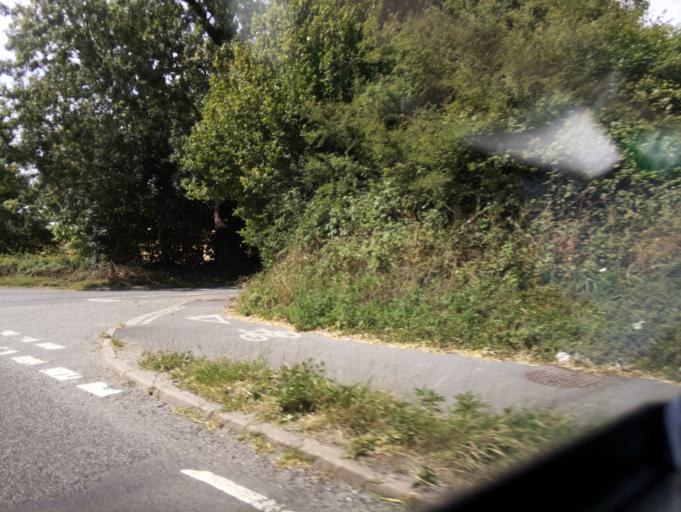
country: GB
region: England
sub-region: Dorset
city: Dorchester
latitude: 50.7356
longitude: -2.4703
